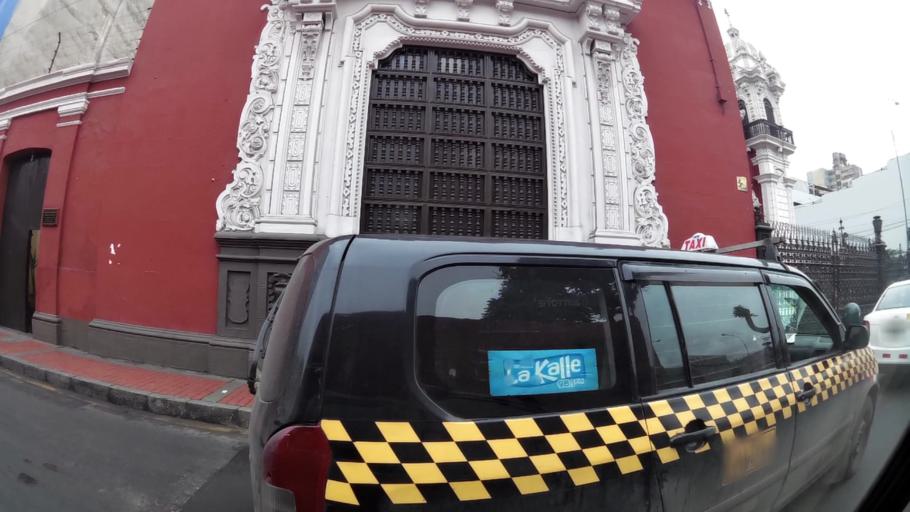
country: PE
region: Lima
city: Lima
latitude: -12.0473
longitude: -77.0366
